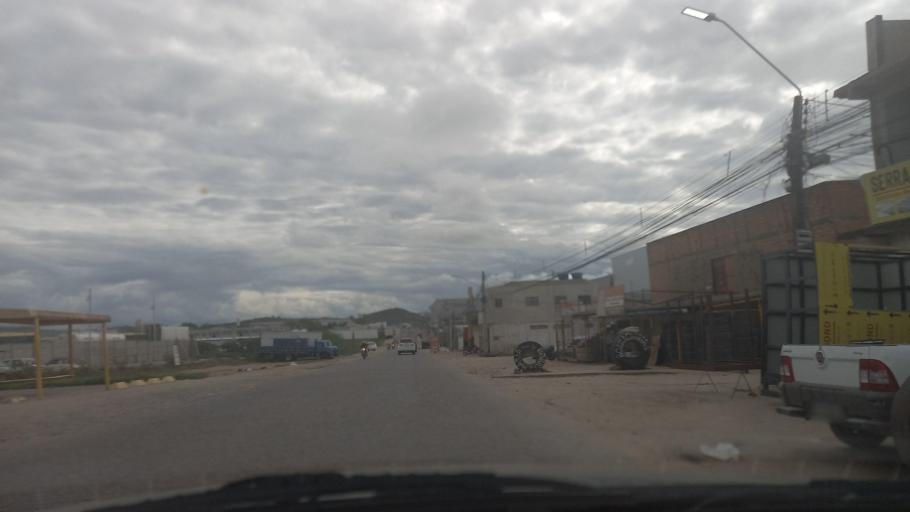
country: BR
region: Pernambuco
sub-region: Caruaru
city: Caruaru
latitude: -8.2881
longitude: -36.0075
